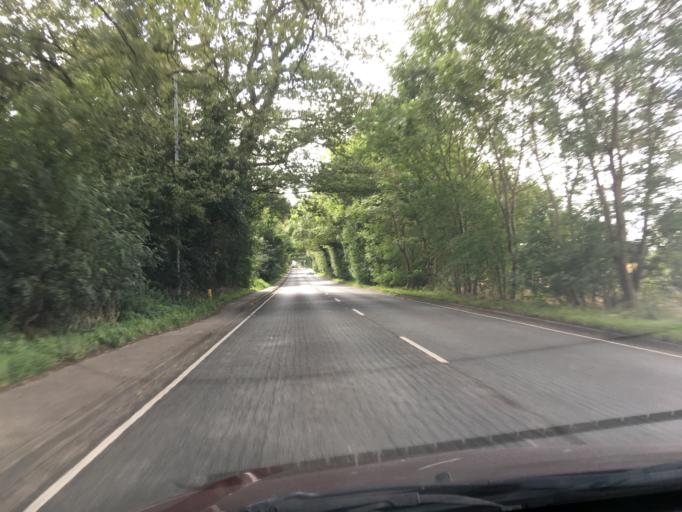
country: GB
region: England
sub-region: Warwickshire
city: Royal Leamington Spa
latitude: 52.3079
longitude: -1.5384
